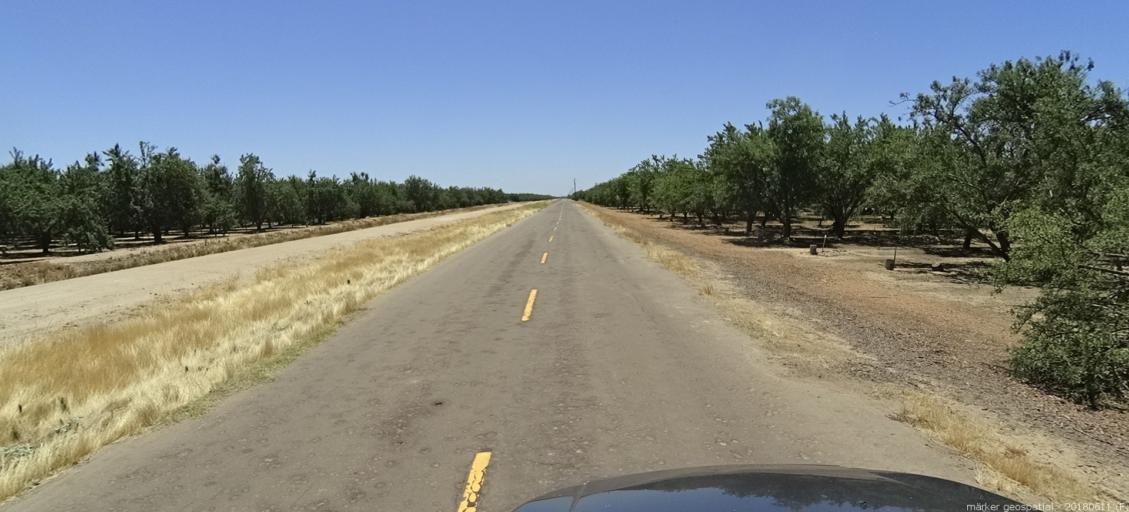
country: US
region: California
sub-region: Madera County
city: Fairmead
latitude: 37.0502
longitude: -120.1841
